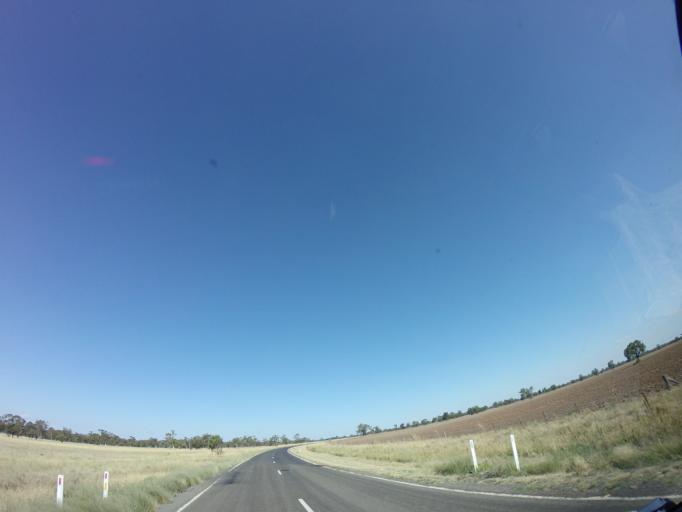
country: AU
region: New South Wales
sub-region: Gilgandra
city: Gilgandra
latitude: -31.6676
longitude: 148.2177
